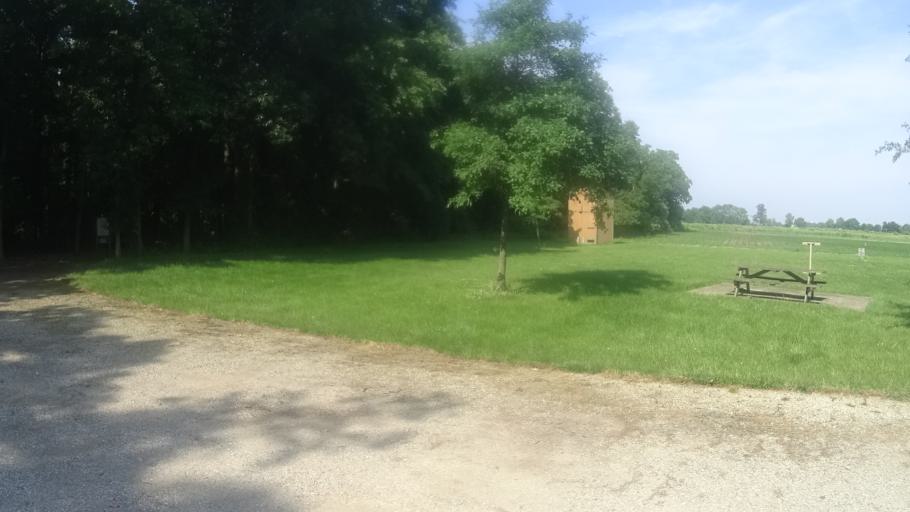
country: US
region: Ohio
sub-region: Huron County
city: Monroeville
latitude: 41.2897
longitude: -82.7586
